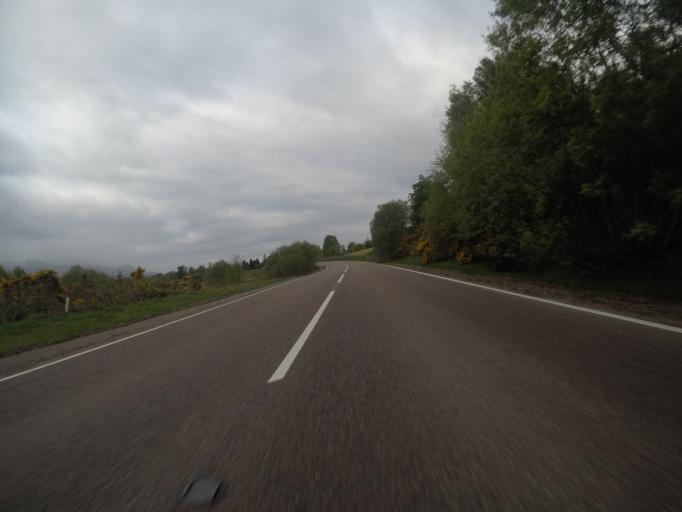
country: GB
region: Scotland
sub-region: Highland
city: Spean Bridge
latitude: 56.8897
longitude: -4.8548
